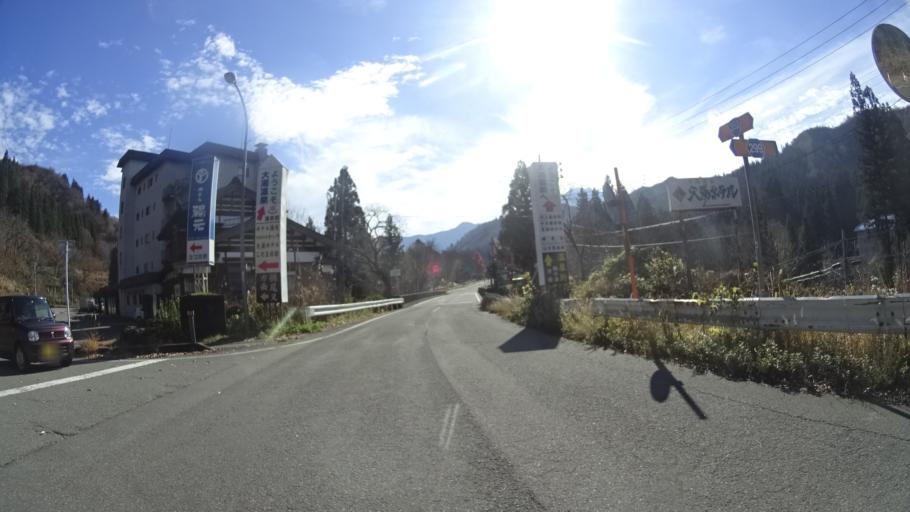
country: JP
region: Niigata
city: Muikamachi
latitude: 37.1999
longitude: 139.0764
